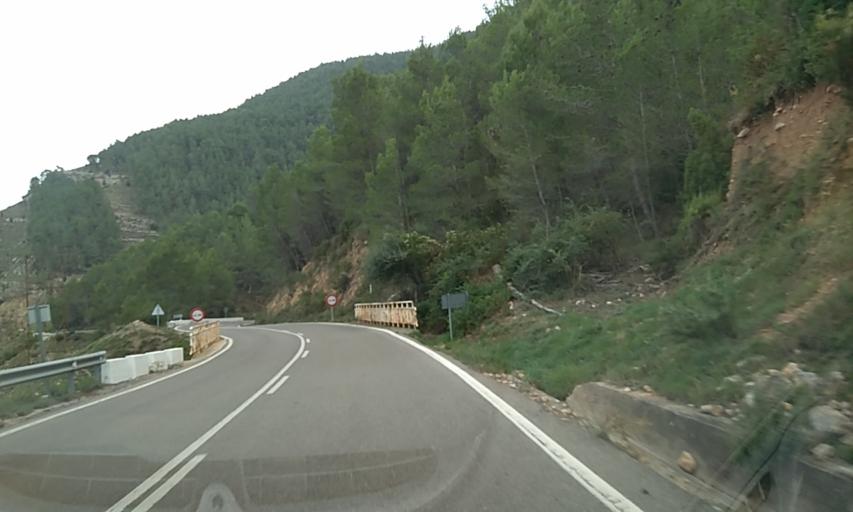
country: ES
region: Valencia
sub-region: Provincia de Castello
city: Montanejos
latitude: 40.0839
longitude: -0.5493
